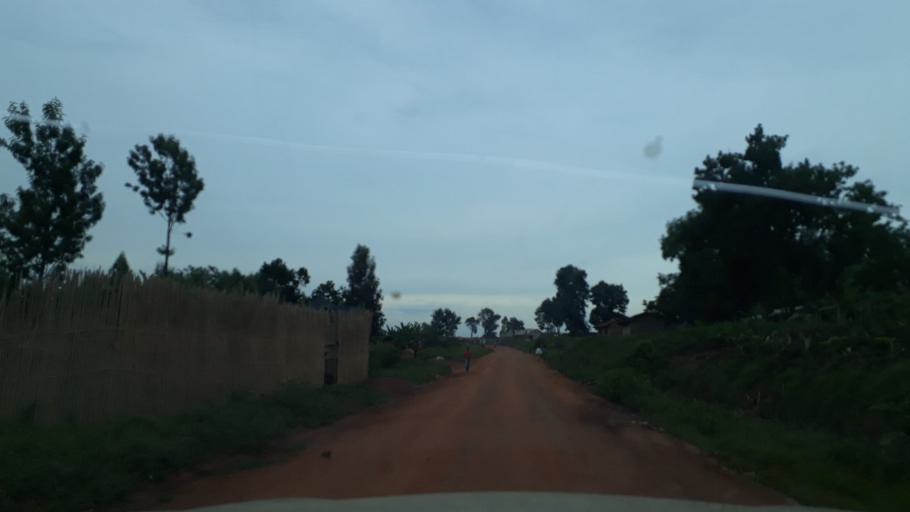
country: UG
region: Northern Region
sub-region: Zombo District
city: Paidha
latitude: 2.1701
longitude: 30.7019
